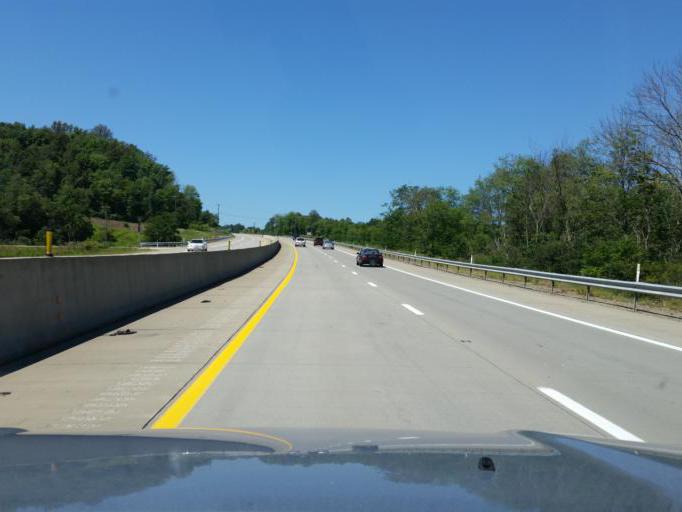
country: US
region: Pennsylvania
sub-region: Indiana County
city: Blairsville
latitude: 40.4216
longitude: -79.3558
